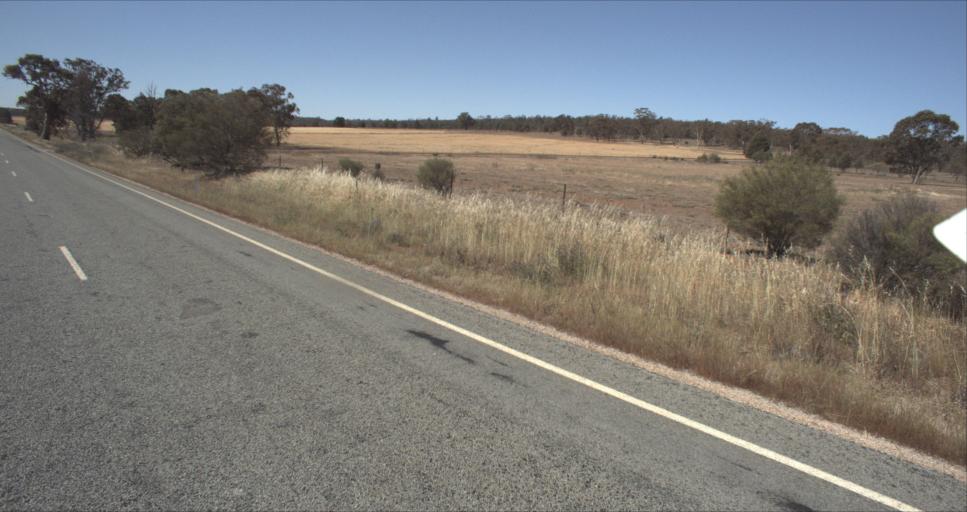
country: AU
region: New South Wales
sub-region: Leeton
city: Leeton
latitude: -34.4582
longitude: 146.4382
